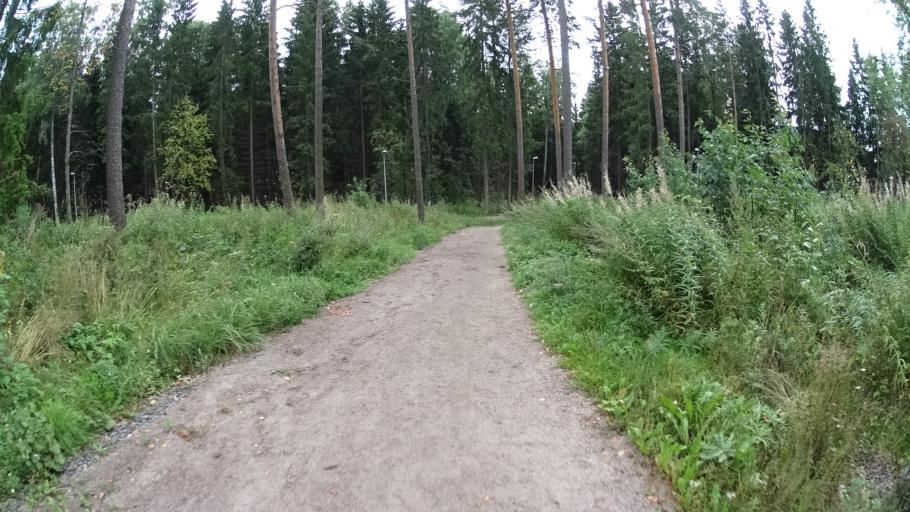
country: FI
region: Uusimaa
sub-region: Helsinki
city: Helsinki
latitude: 60.2297
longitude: 24.9028
